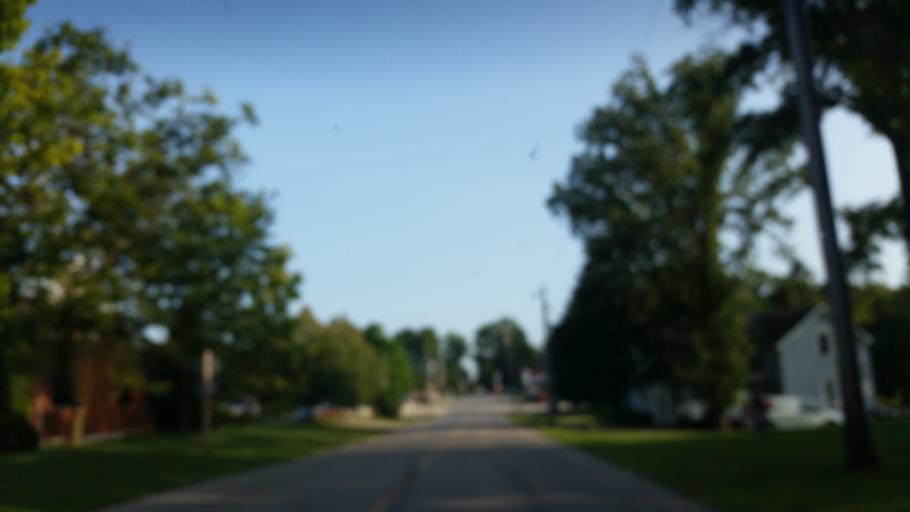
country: CA
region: Ontario
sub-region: Oxford County
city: Woodstock
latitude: 43.0252
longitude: -80.6538
